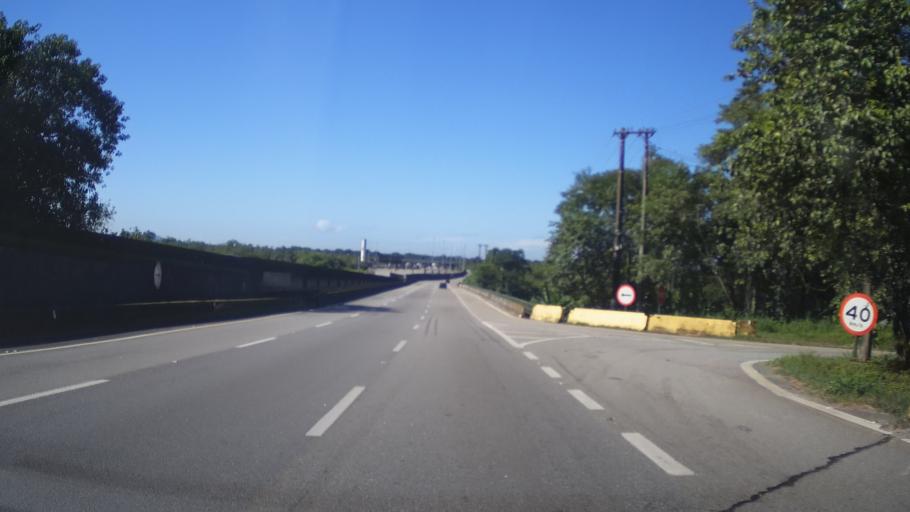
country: BR
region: Sao Paulo
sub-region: Cubatao
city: Cubatao
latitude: -23.9337
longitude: -46.4653
